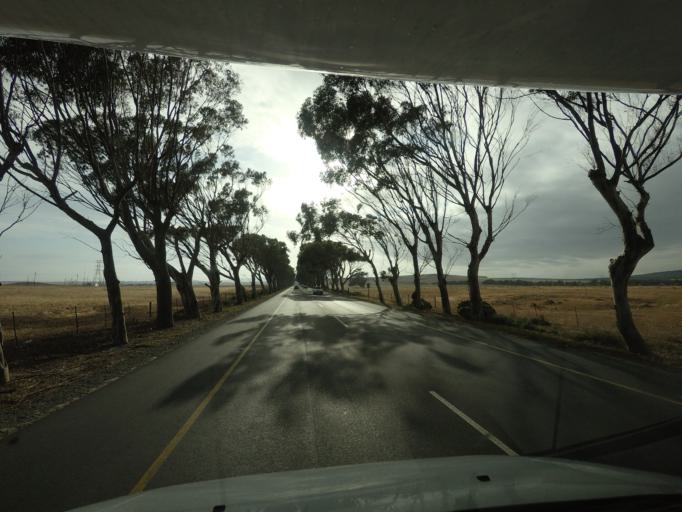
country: ZA
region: Western Cape
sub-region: City of Cape Town
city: Sunset Beach
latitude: -33.7254
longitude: 18.4636
